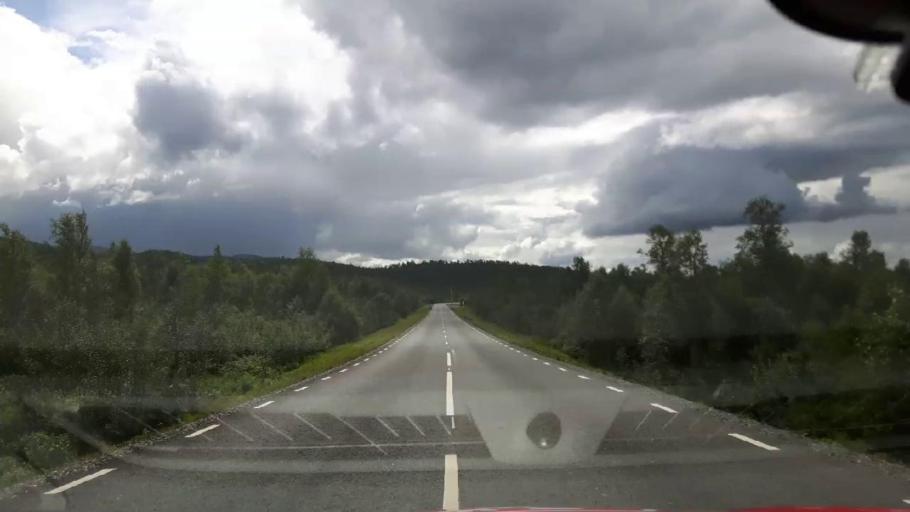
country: NO
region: Nordland
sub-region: Hattfjelldal
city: Hattfjelldal
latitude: 64.9826
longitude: 14.2129
